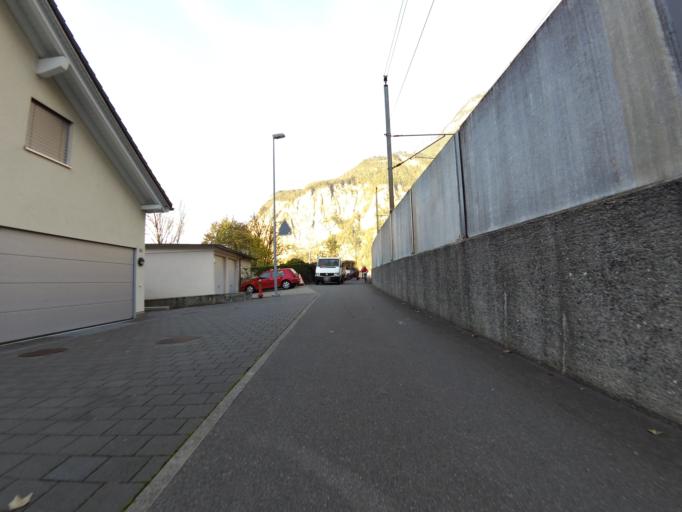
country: CH
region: Uri
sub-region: Uri
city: Flueelen
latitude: 46.9120
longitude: 8.6216
